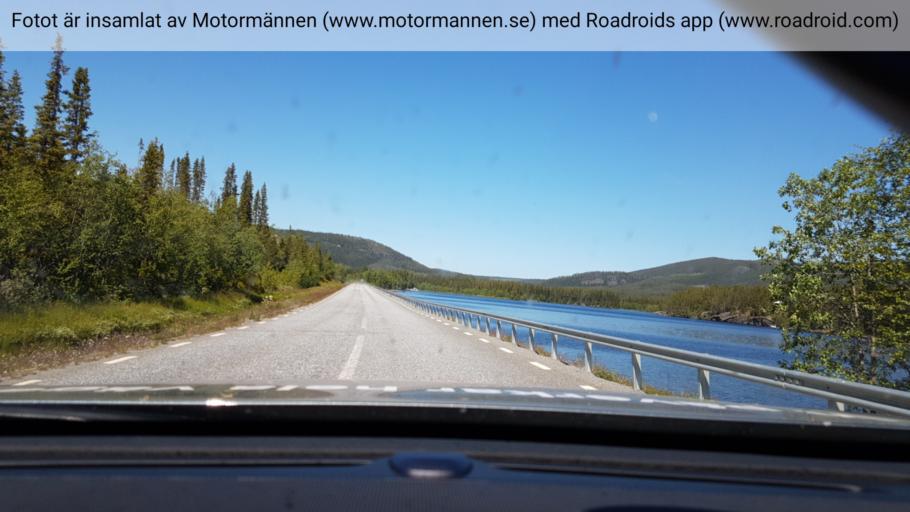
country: SE
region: Vaesterbotten
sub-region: Vilhelmina Kommun
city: Sjoberg
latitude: 64.9223
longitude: 15.8683
